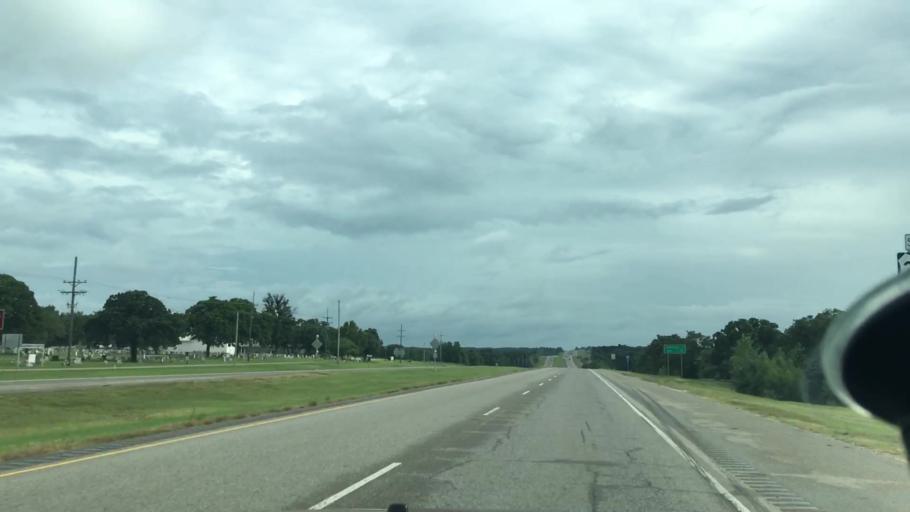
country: US
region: Oklahoma
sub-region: Seminole County
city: Seminole
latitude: 35.3477
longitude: -96.6719
